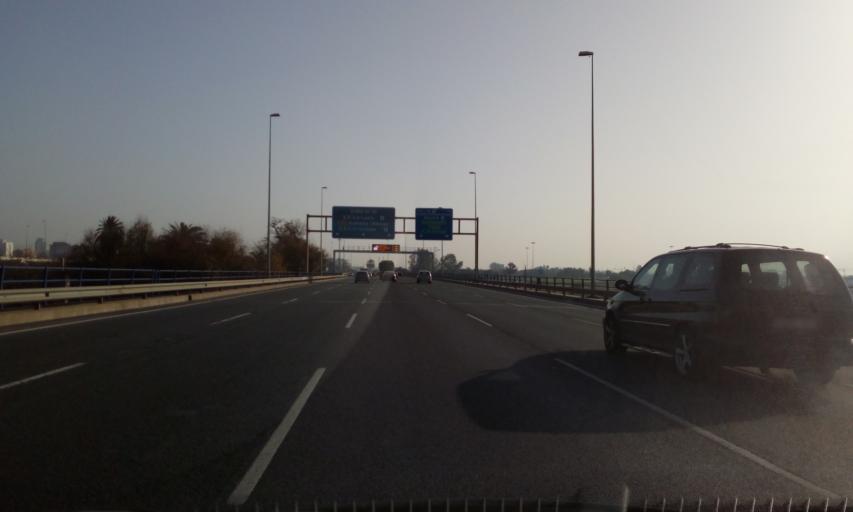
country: ES
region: Andalusia
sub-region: Provincia de Sevilla
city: San Juan de Aznalfarache
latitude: 37.3714
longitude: -6.0224
